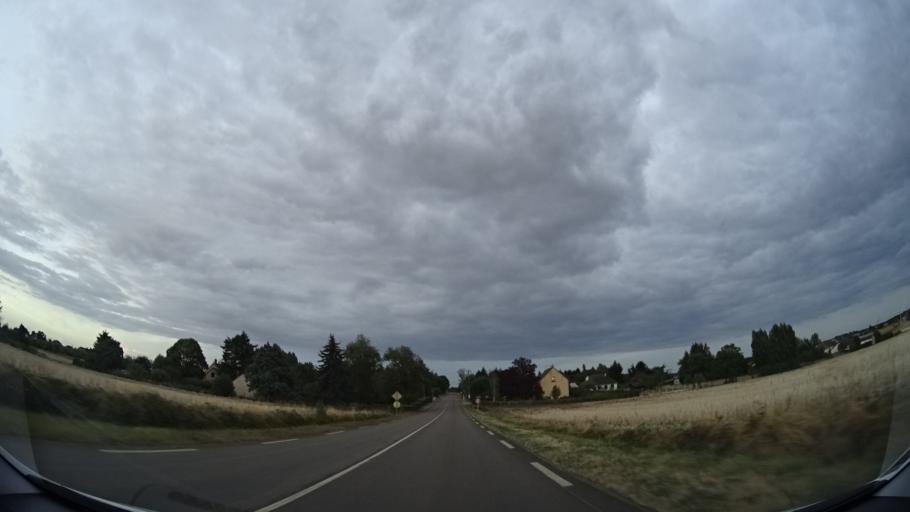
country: FR
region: Bourgogne
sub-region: Departement de l'Yonne
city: Charny
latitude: 47.9386
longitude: 3.1499
